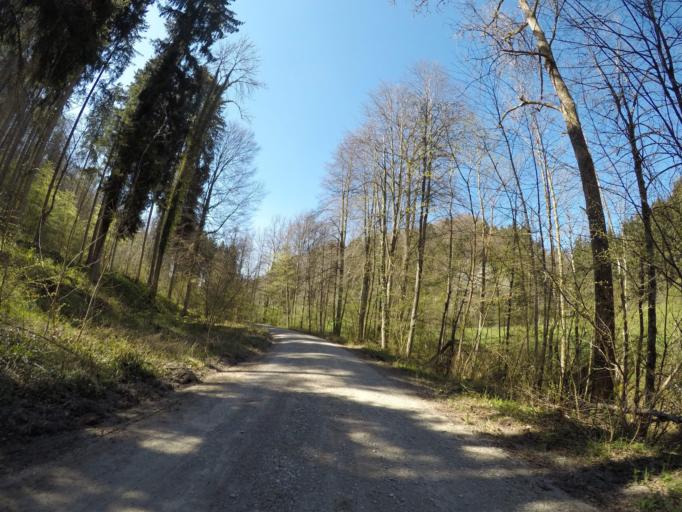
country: DE
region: Baden-Wuerttemberg
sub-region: Tuebingen Region
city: Horgenzell
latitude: 47.7997
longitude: 9.4607
